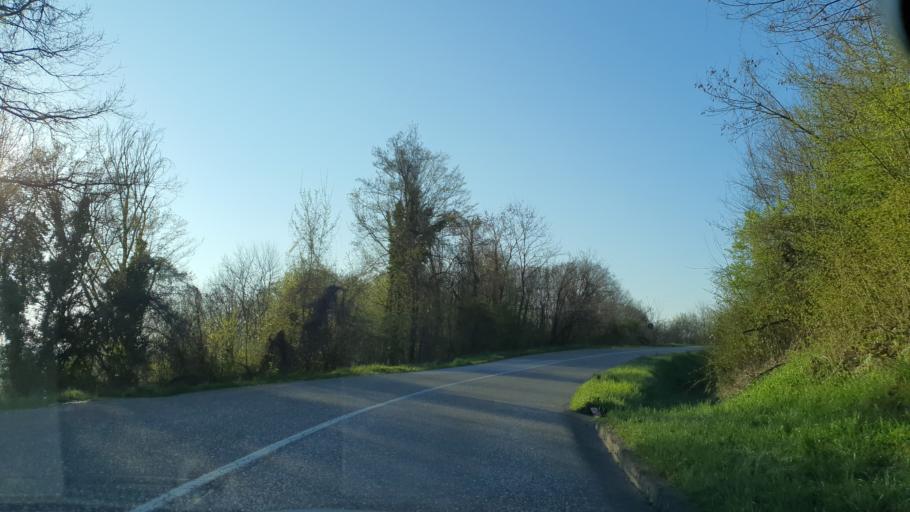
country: RS
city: Bukor
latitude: 44.4713
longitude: 19.4899
